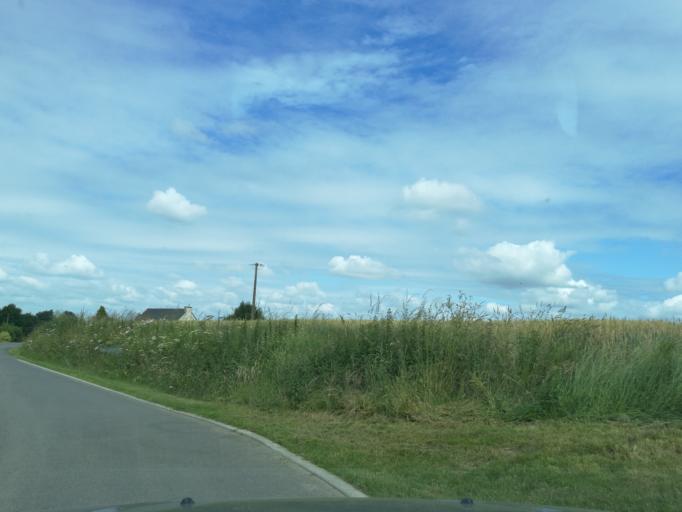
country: FR
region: Brittany
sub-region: Departement d'Ille-et-Vilaine
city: Bedee
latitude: 48.1631
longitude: -1.9803
